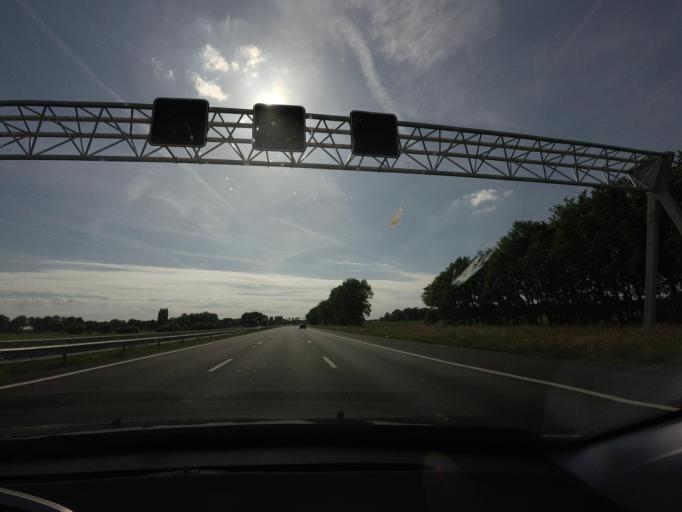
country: NL
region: Gelderland
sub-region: Gemeente Lochem
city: Laren
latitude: 52.2478
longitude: 6.3864
